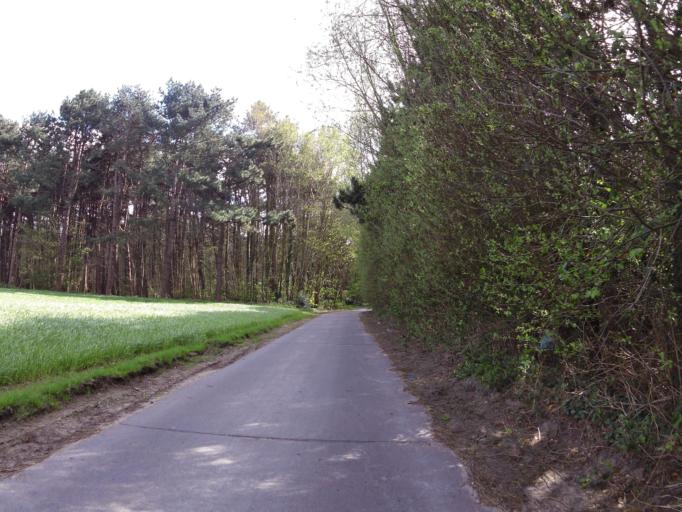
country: BE
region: Flanders
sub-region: Provincie West-Vlaanderen
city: Jabbeke
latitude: 51.1860
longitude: 3.1251
